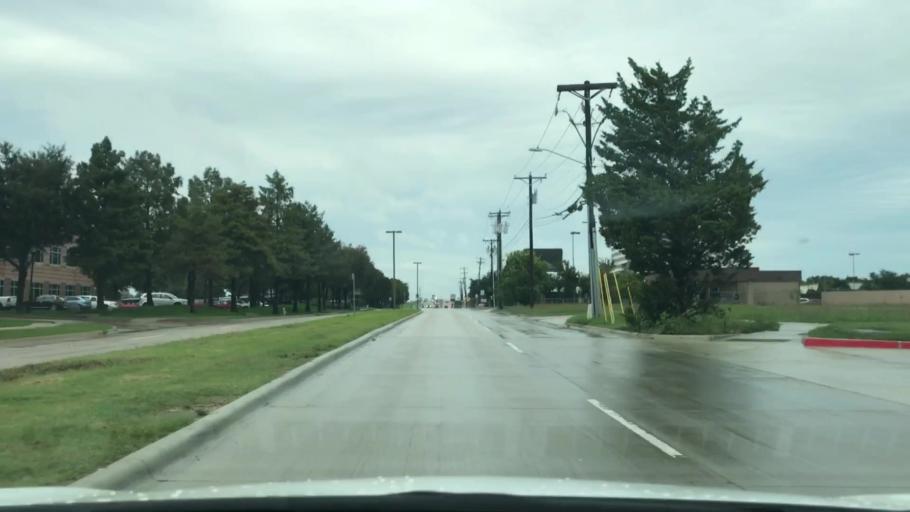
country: US
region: Texas
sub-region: Dallas County
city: Coppell
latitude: 32.9104
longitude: -97.0080
